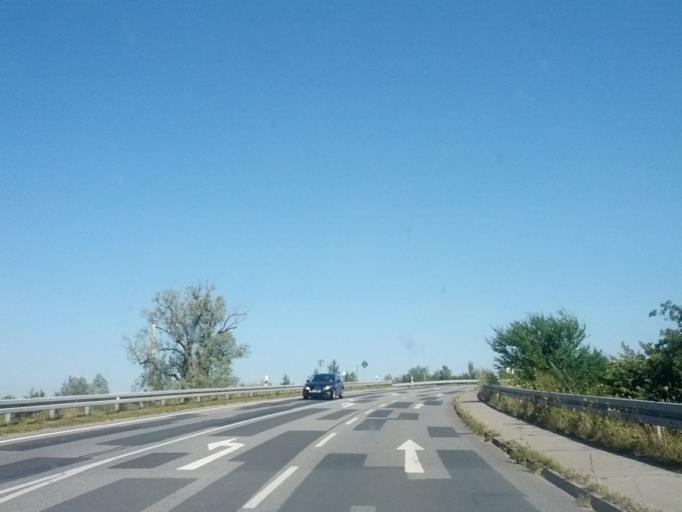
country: DE
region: Mecklenburg-Vorpommern
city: Sagard
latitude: 54.4863
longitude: 13.5769
